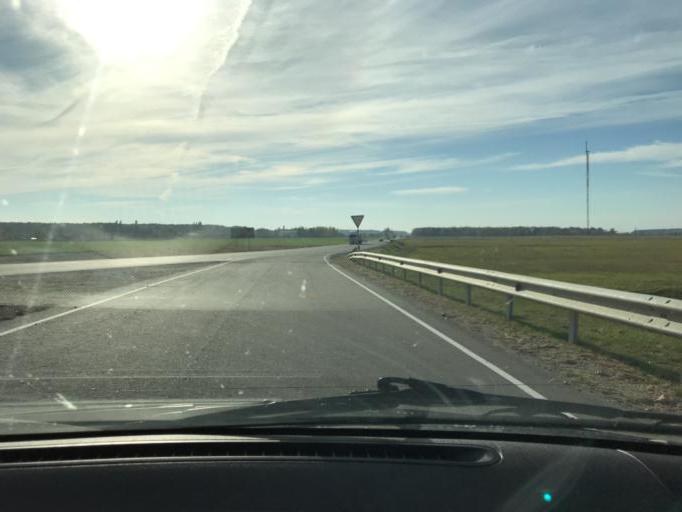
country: BY
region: Brest
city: Asnyezhytsy
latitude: 52.1830
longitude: 26.0744
